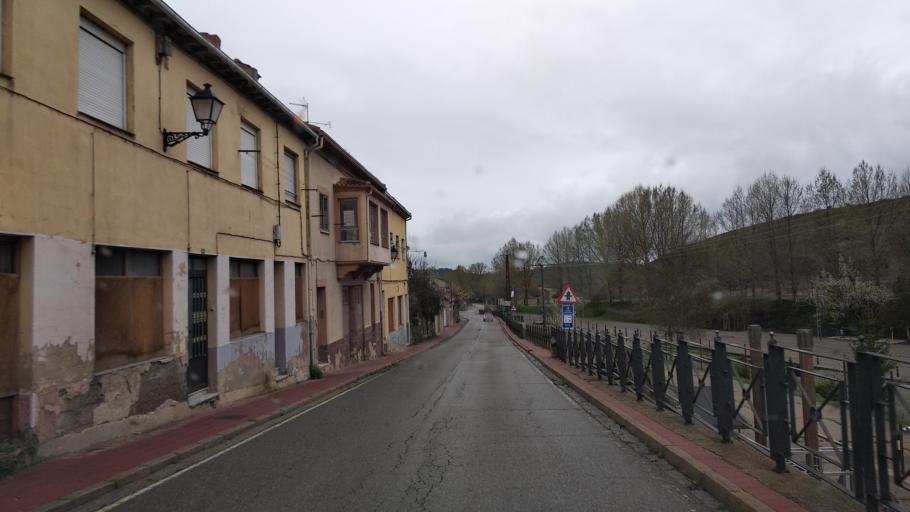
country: ES
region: Castille and Leon
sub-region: Provincia de Palencia
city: Barruelo de Santullan
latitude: 42.9037
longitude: -4.2876
